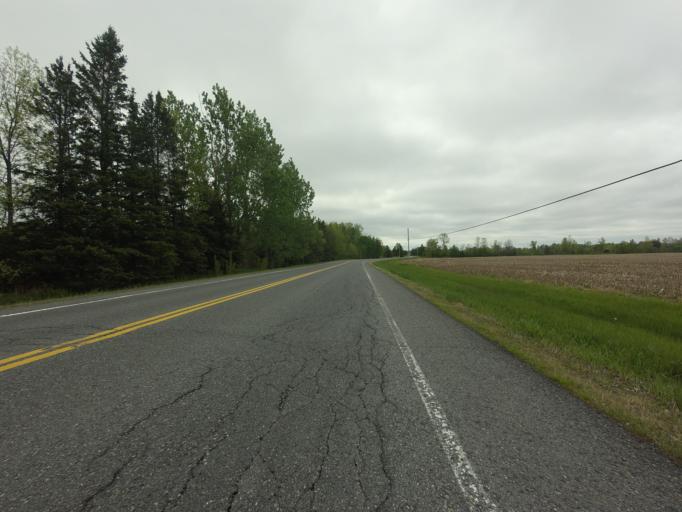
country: CA
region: Ontario
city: Casselman
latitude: 45.0538
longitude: -75.2005
